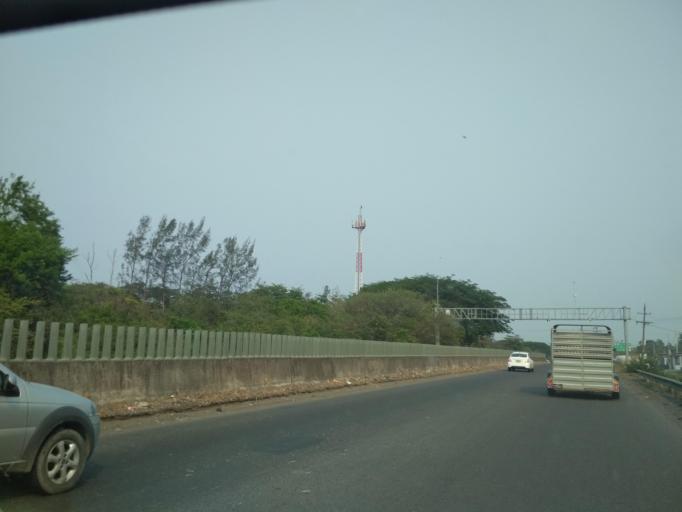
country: MX
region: Veracruz
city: El Tejar
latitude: 19.0877
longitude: -96.2016
